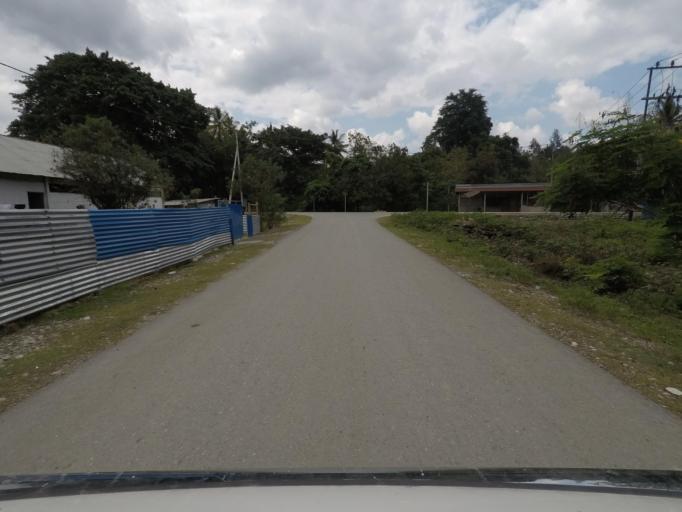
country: TL
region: Viqueque
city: Viqueque
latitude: -8.8824
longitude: 126.3755
